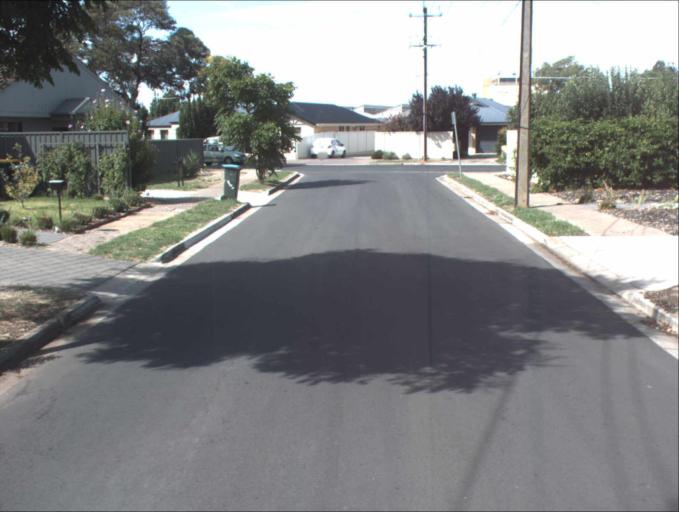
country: AU
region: South Australia
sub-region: Port Adelaide Enfield
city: Klemzig
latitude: -34.8681
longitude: 138.6445
